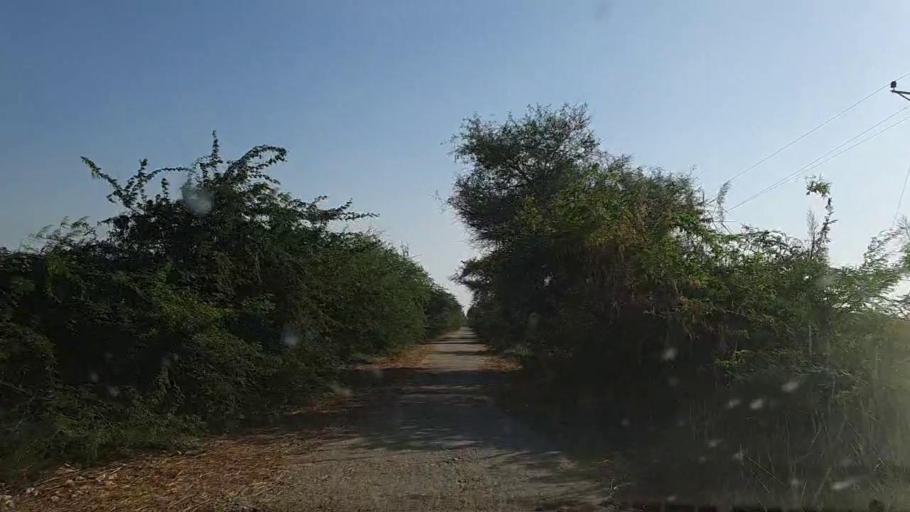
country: PK
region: Sindh
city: Daro Mehar
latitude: 24.6496
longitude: 68.0750
